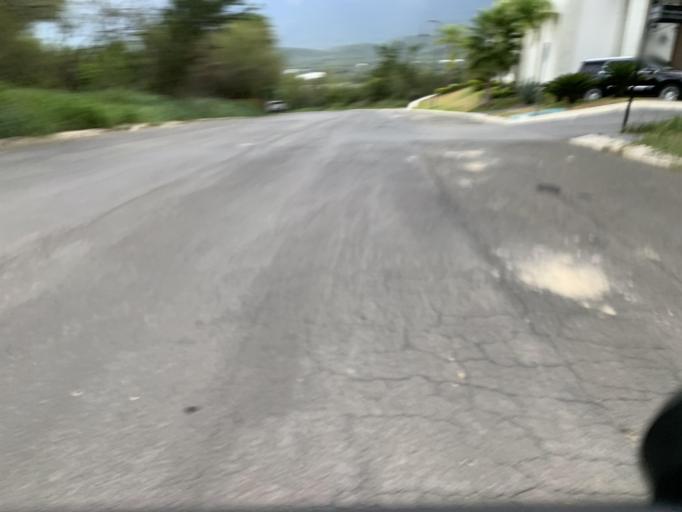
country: MX
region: Nuevo Leon
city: Santiago
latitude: 25.5078
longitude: -100.1801
